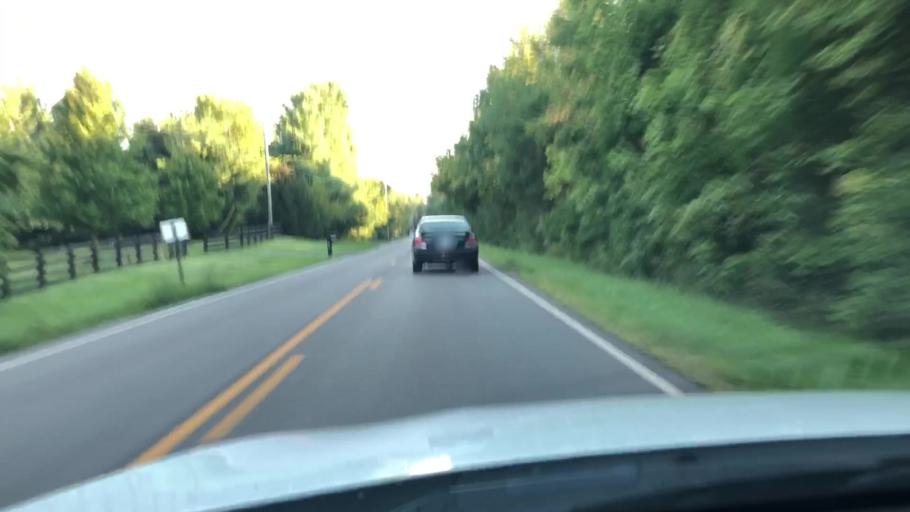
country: US
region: Kentucky
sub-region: Jefferson County
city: Middletown
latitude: 38.2161
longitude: -85.5076
